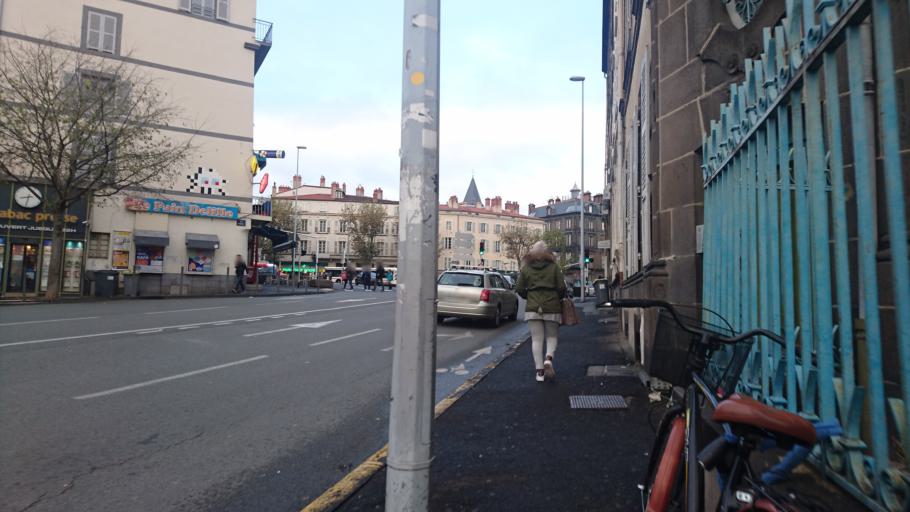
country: FR
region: Auvergne
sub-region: Departement du Puy-de-Dome
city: Clermont-Ferrand
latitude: 45.7797
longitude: 3.0920
